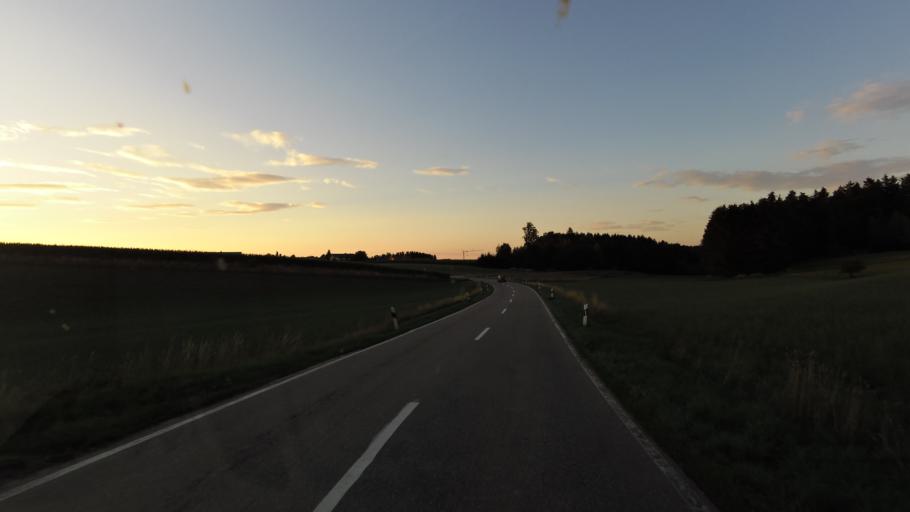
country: DE
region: Bavaria
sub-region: Upper Bavaria
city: Taufkirchen
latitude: 48.1248
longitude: 12.4635
